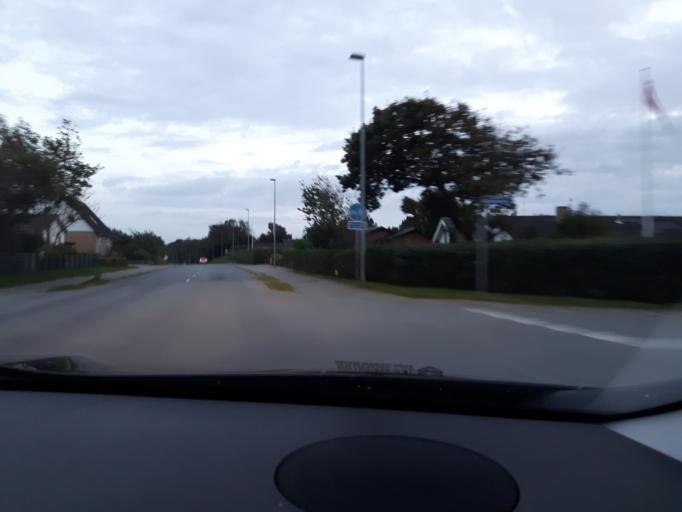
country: DK
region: North Denmark
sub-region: Hjorring Kommune
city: Hirtshals
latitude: 57.5317
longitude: 9.9466
